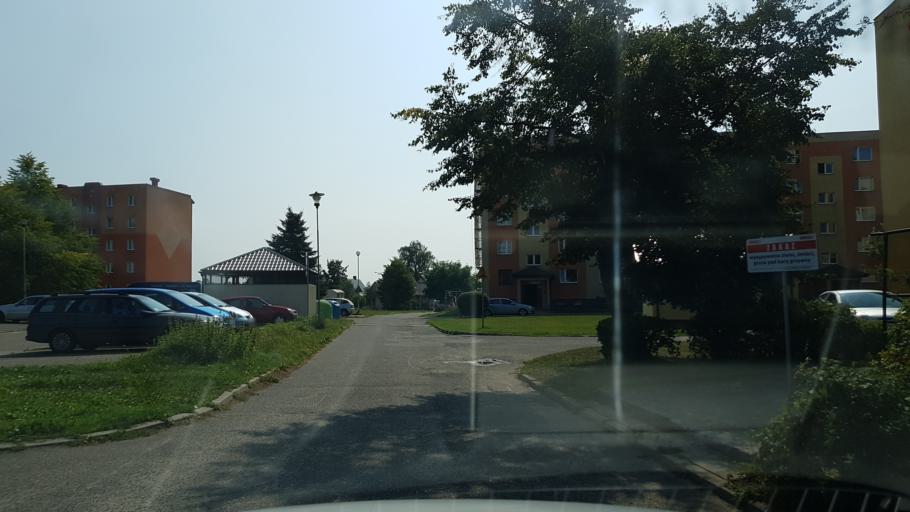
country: PL
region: West Pomeranian Voivodeship
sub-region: Powiat slawienski
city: Darlowo
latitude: 54.4231
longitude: 16.4203
